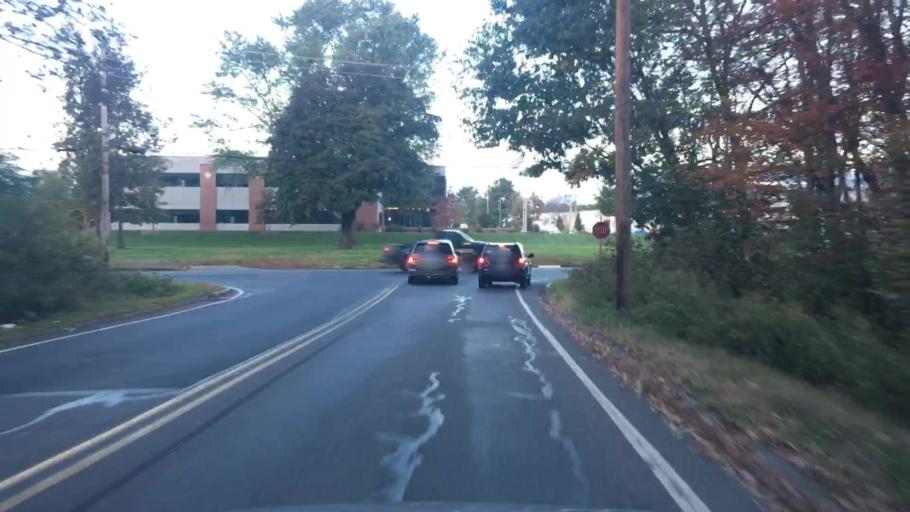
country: US
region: Massachusetts
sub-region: Hampden County
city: East Longmeadow
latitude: 42.0413
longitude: -72.5173
